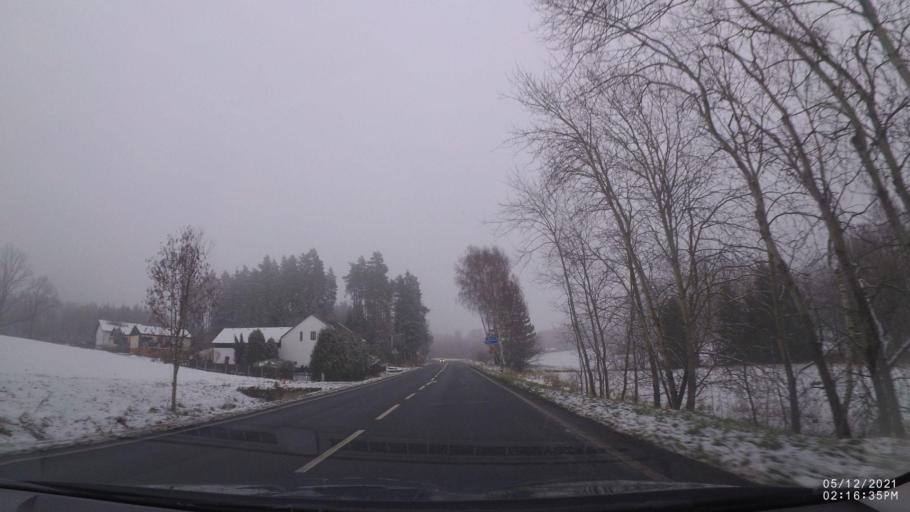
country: CZ
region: Kralovehradecky
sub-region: Okres Nachod
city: Cerveny Kostelec
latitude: 50.4688
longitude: 16.1166
